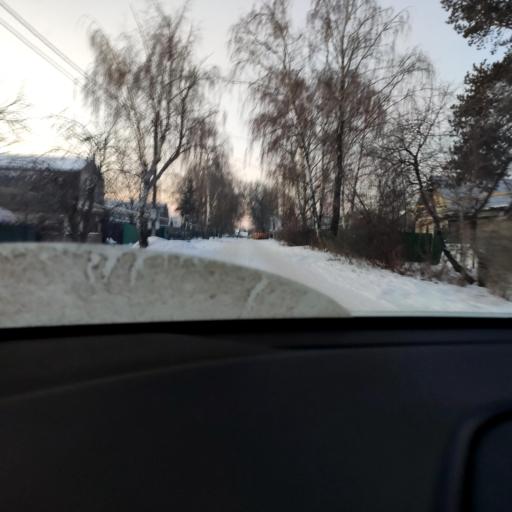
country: RU
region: Tatarstan
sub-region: Gorod Kazan'
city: Kazan
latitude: 55.7423
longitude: 49.0987
